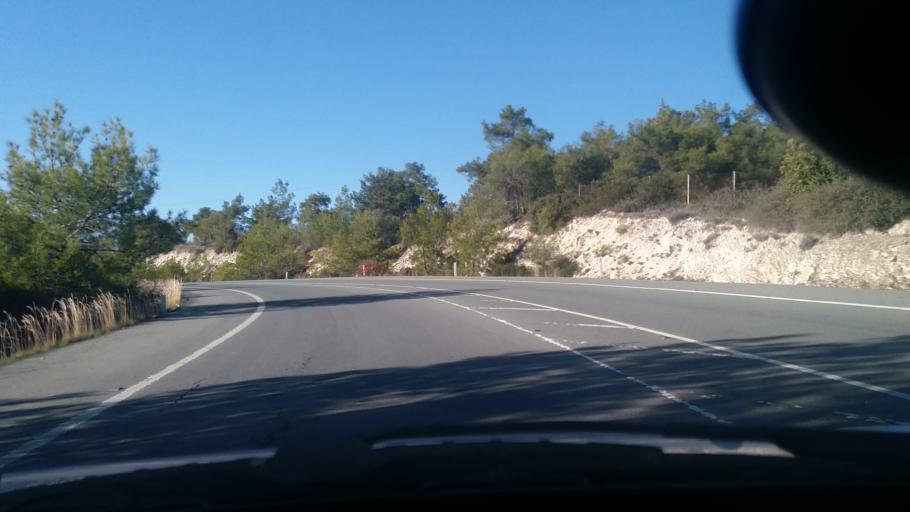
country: CY
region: Larnaka
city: Kofinou
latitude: 34.8546
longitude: 33.4469
